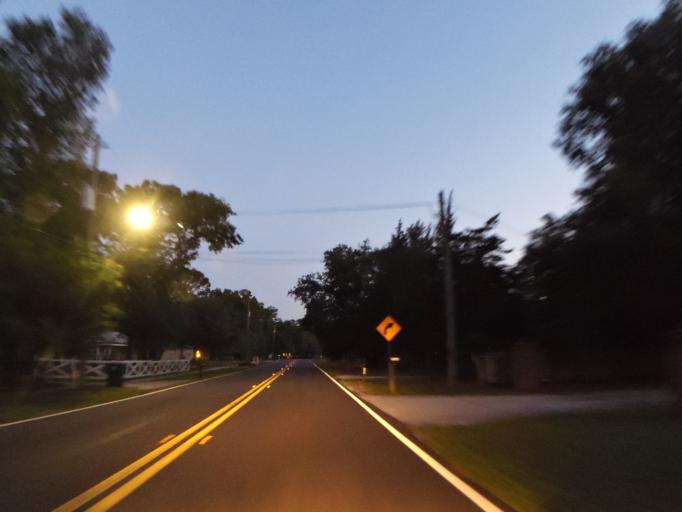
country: US
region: Florida
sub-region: Duval County
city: Jacksonville
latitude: 30.3012
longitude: -81.5406
